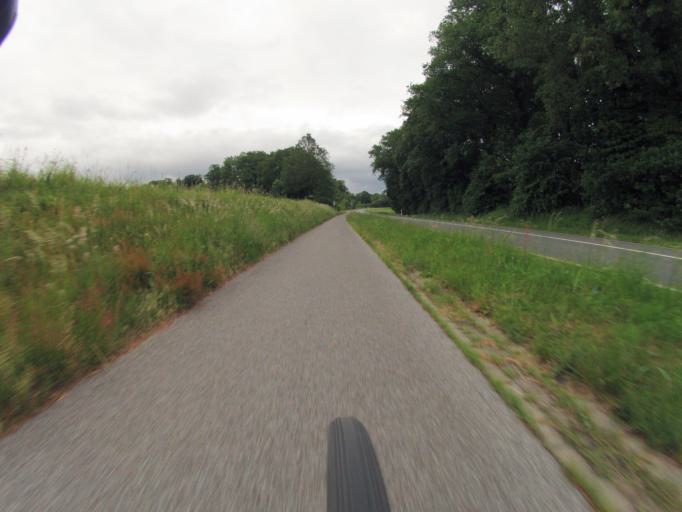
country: DE
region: North Rhine-Westphalia
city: Emsdetten
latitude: 52.2056
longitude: 7.5542
